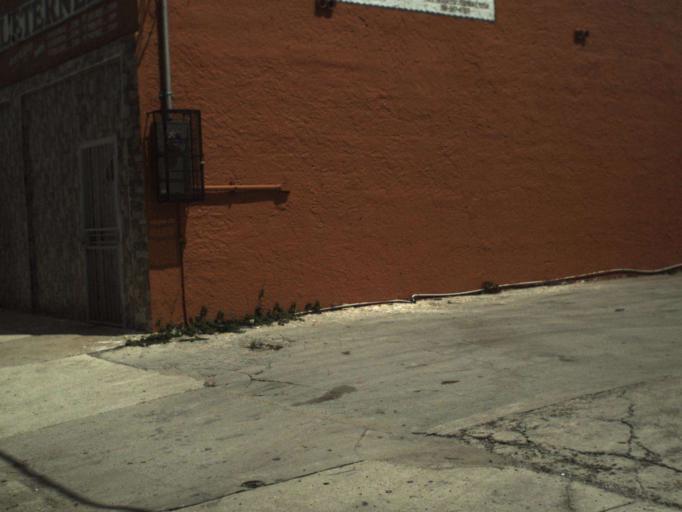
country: US
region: Florida
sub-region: Miami-Dade County
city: Allapattah
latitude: 25.7984
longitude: -80.2071
